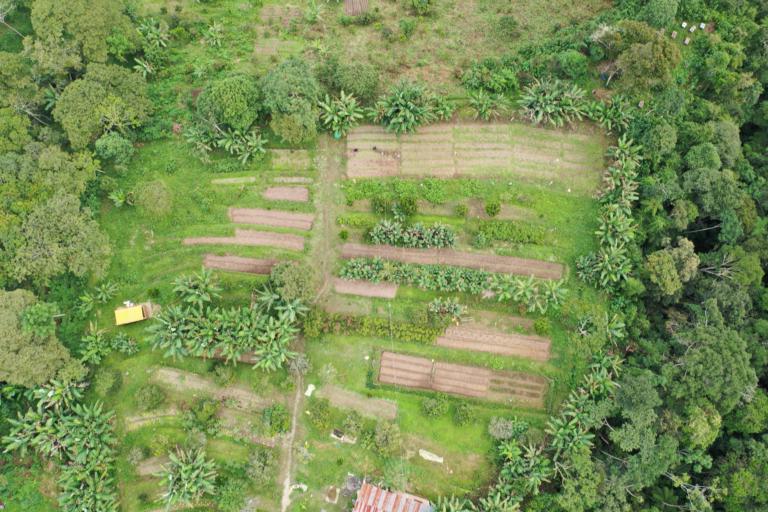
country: BO
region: La Paz
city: Coroico
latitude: -16.2588
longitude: -67.6929
